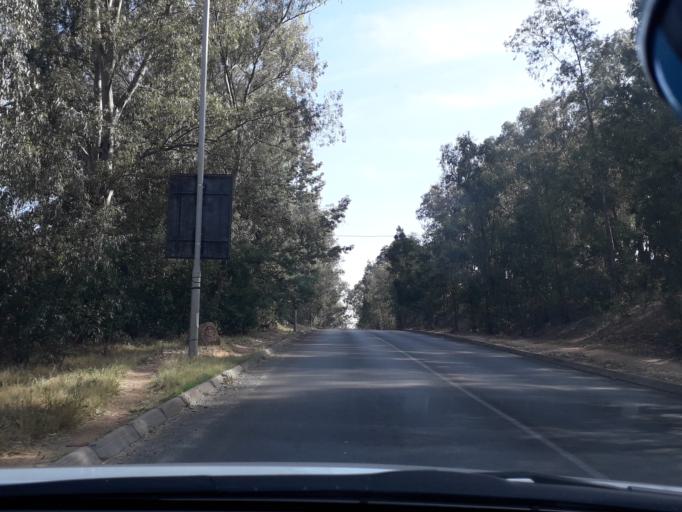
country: ZA
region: Gauteng
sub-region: City of Johannesburg Metropolitan Municipality
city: Roodepoort
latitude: -26.1094
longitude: 27.8973
